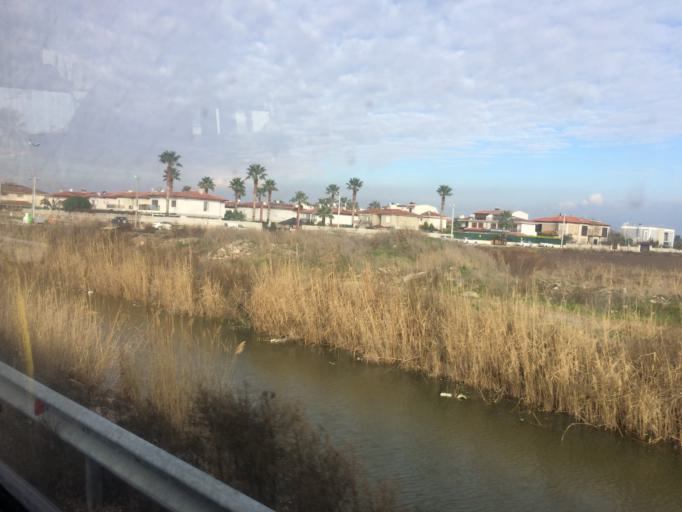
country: TR
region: Izmir
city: Menemen
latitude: 38.5009
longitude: 26.9600
